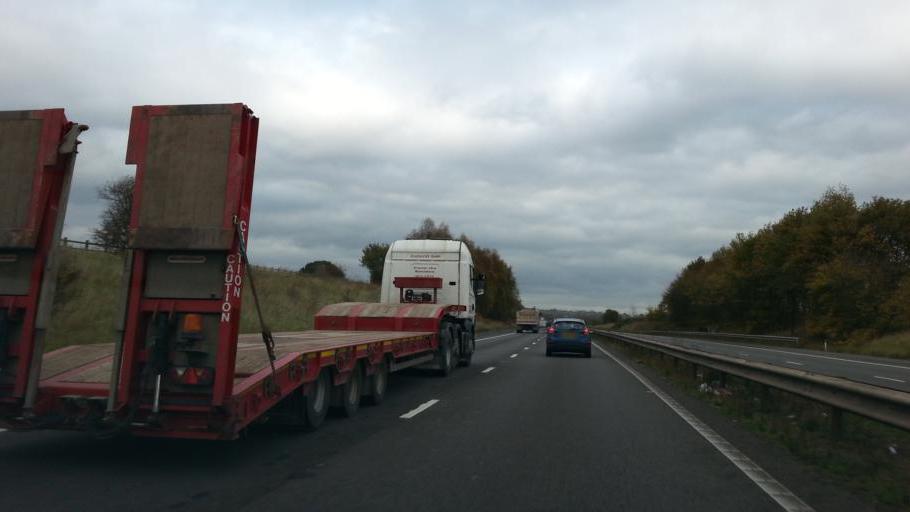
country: GB
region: England
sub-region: Derbyshire
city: Netherseal
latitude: 52.6410
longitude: -1.6003
